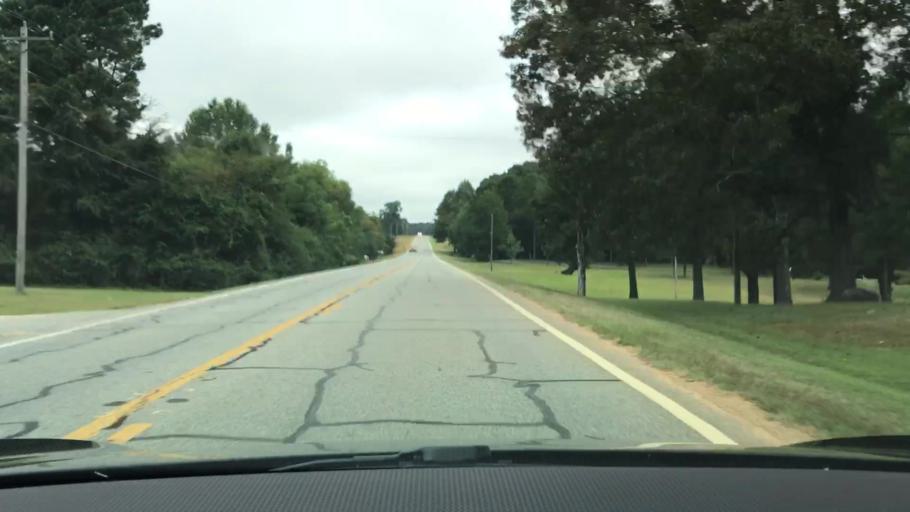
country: US
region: Georgia
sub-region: Oconee County
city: Watkinsville
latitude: 33.8000
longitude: -83.3366
